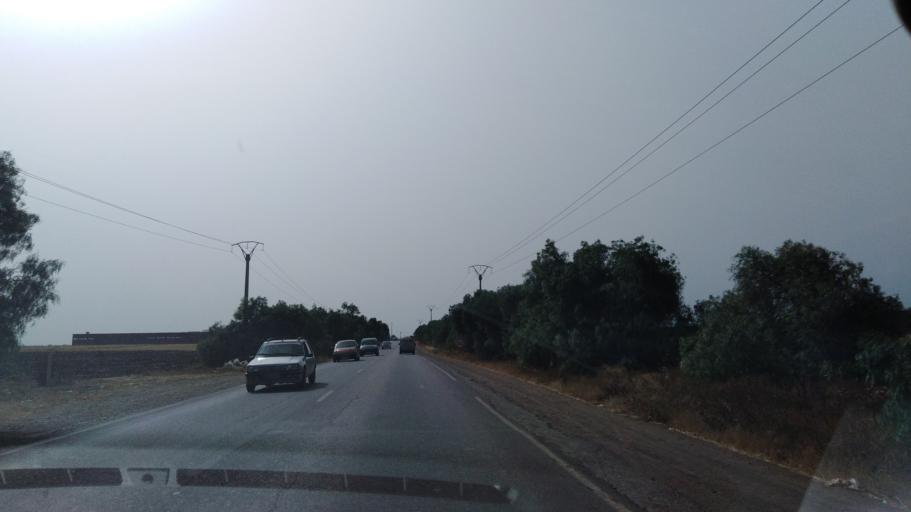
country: MA
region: Chaouia-Ouardigha
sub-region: Settat Province
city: Berrechid
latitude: 33.2440
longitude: -7.5508
